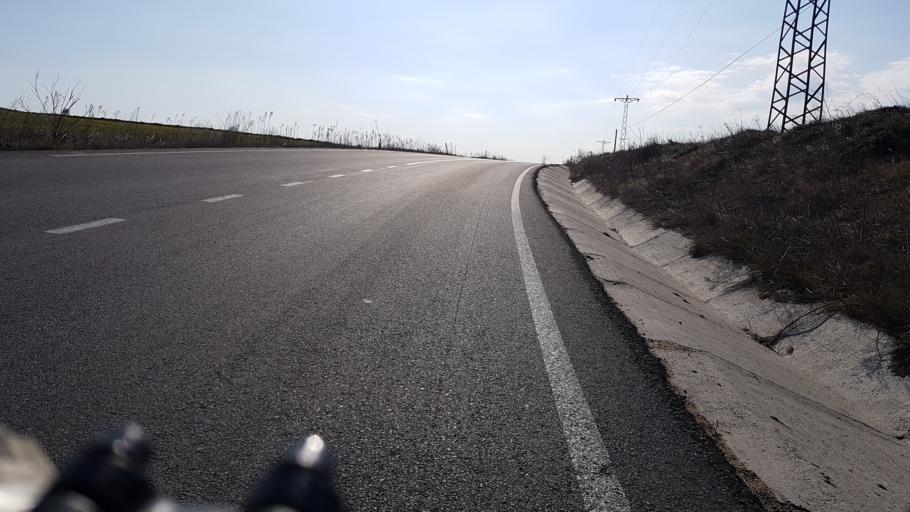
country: TR
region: Tekirdag
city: Velimese
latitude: 41.3550
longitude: 27.8482
